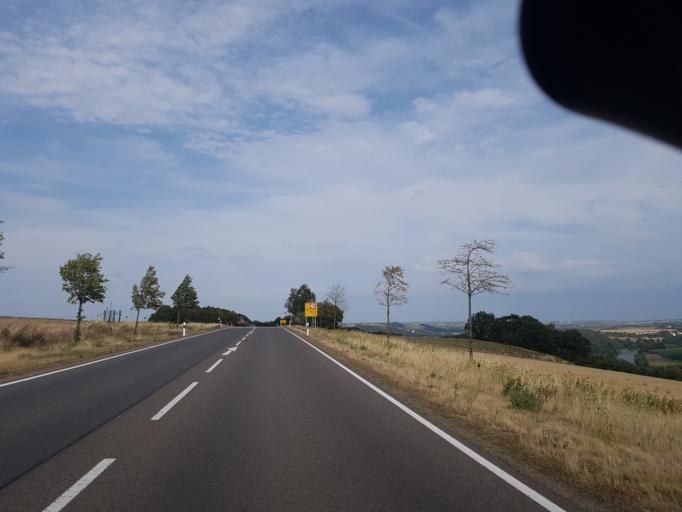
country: DE
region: Saxony
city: Hartha
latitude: 51.1181
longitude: 13.0047
